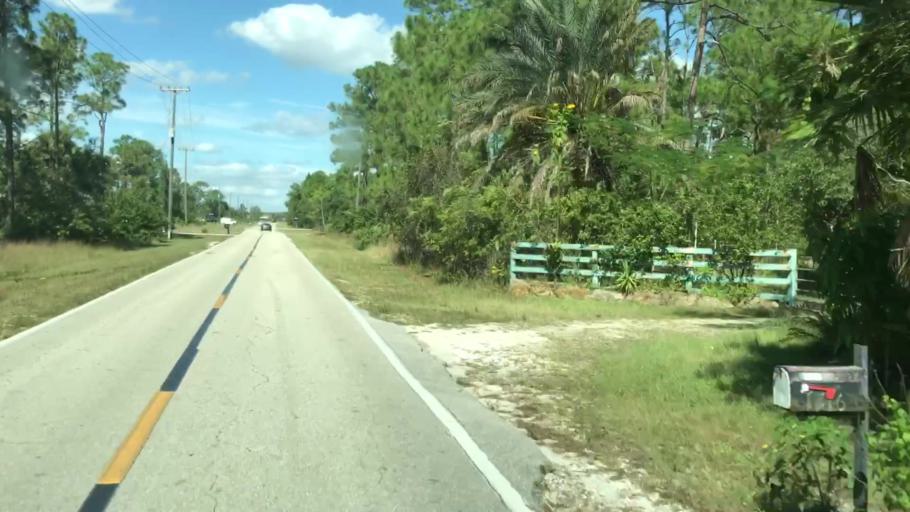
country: US
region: Florida
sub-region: Lee County
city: Lehigh Acres
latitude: 26.6641
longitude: -81.6256
